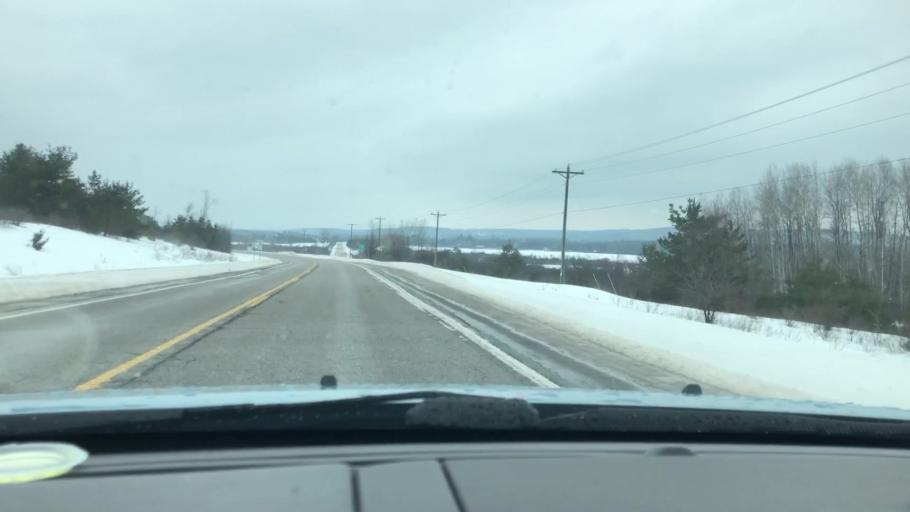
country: US
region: Michigan
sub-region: Charlevoix County
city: East Jordan
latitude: 45.1170
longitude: -85.1295
